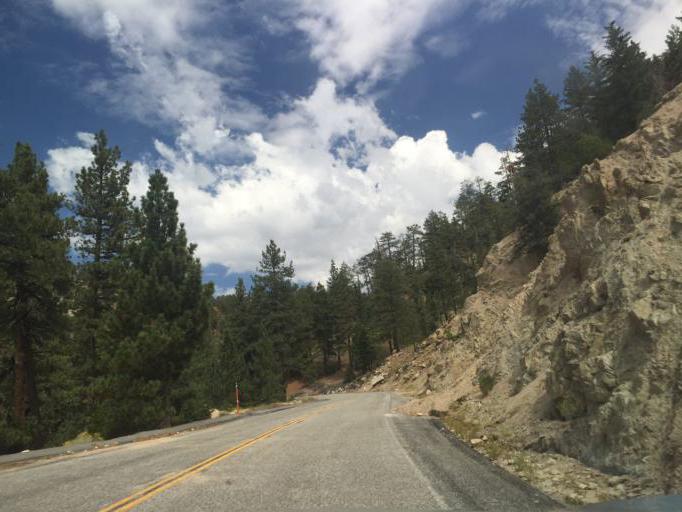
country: US
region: California
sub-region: Los Angeles County
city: Littlerock
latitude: 34.3493
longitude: -117.9423
